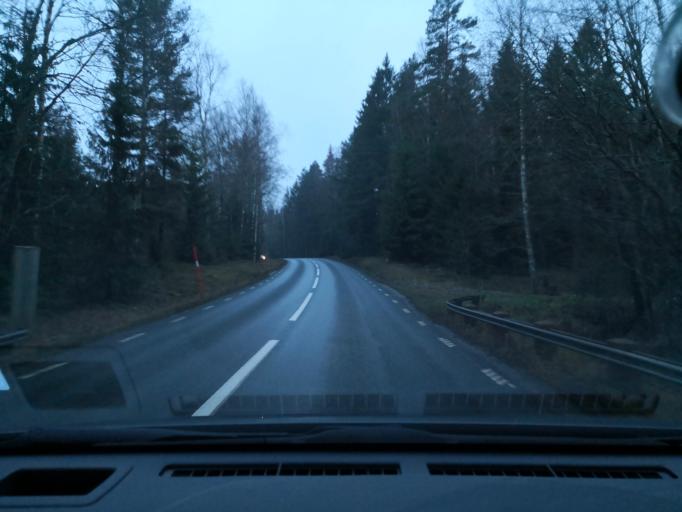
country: SE
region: Soedermanland
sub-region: Eskilstuna Kommun
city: Skogstorp
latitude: 59.2616
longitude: 16.3638
